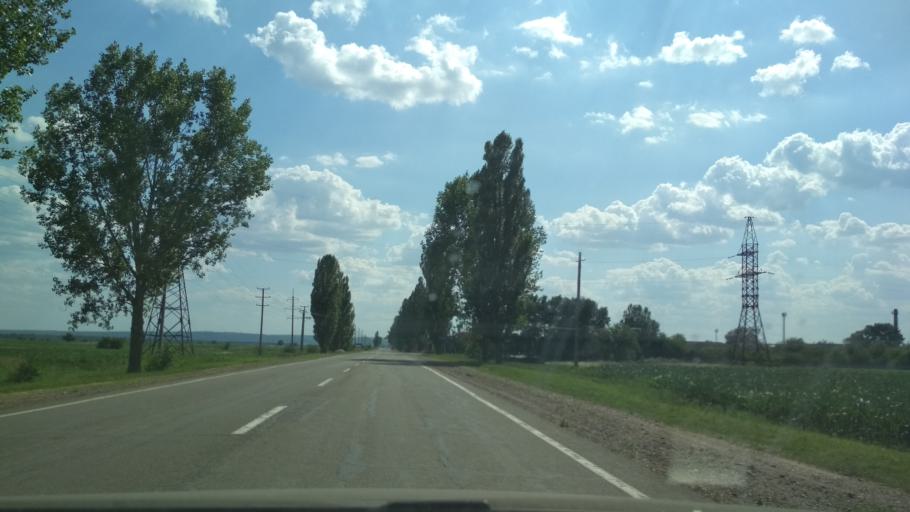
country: MD
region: Criuleni
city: Criuleni
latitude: 47.1541
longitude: 29.1558
